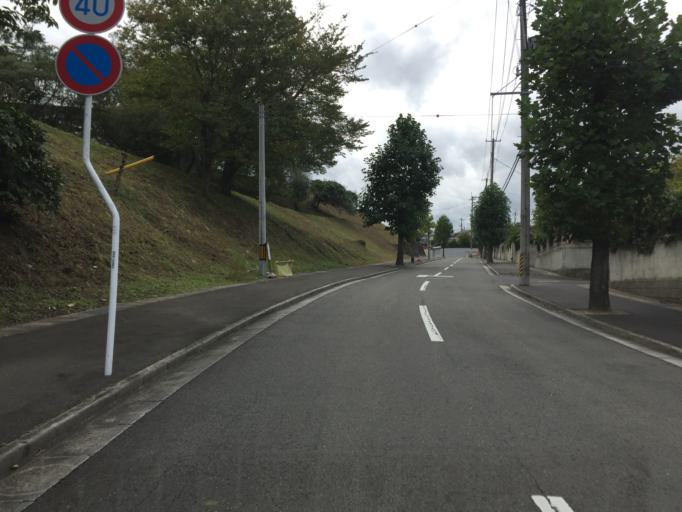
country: JP
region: Fukushima
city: Fukushima-shi
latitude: 37.6966
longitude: 140.4806
